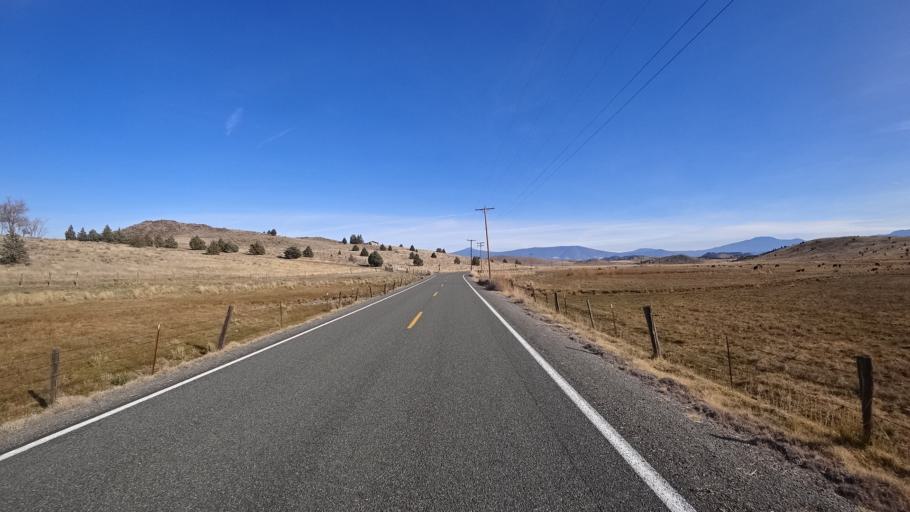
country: US
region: California
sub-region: Siskiyou County
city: Weed
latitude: 41.5362
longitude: -122.5088
